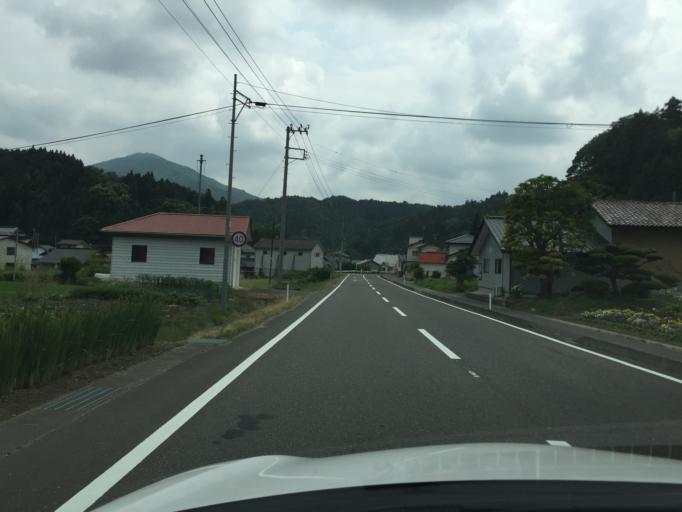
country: JP
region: Fukushima
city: Miharu
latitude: 37.2946
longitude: 140.5392
